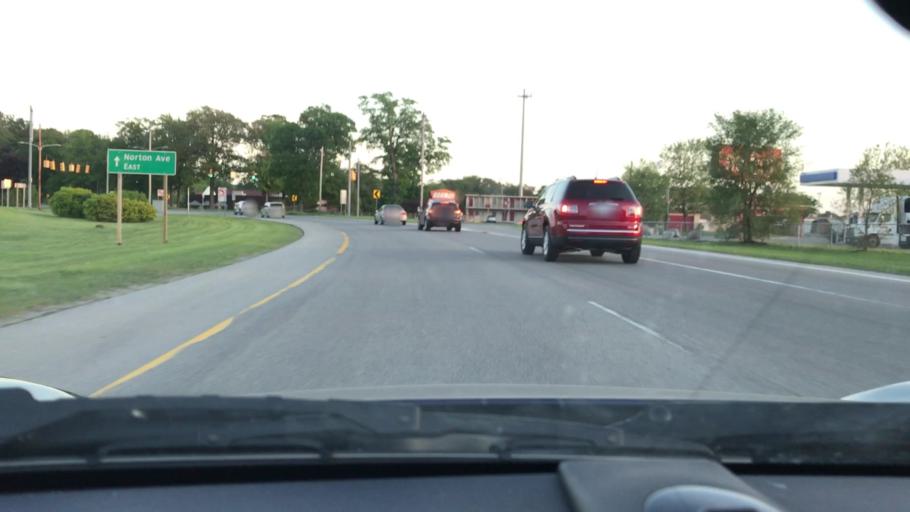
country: US
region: Michigan
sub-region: Muskegon County
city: Roosevelt Park
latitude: 43.1918
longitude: -86.2603
